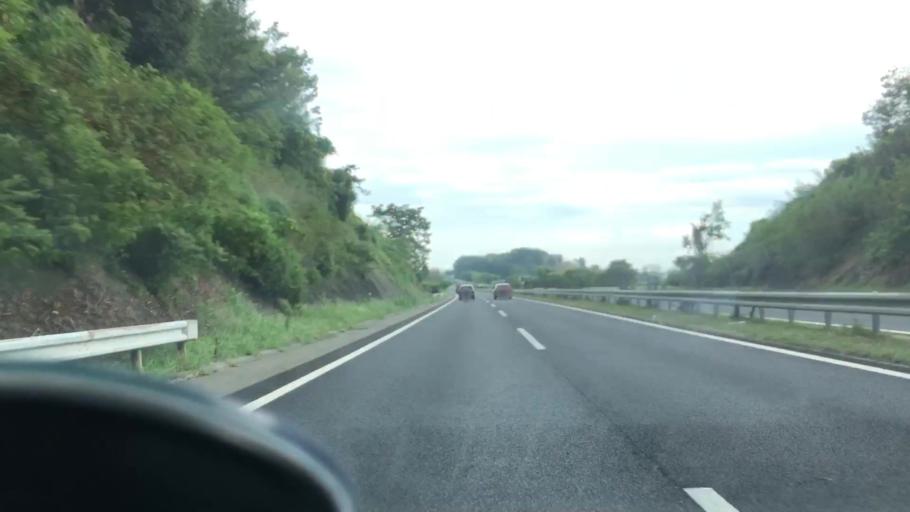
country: JP
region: Hyogo
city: Yashiro
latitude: 34.9370
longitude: 134.8827
